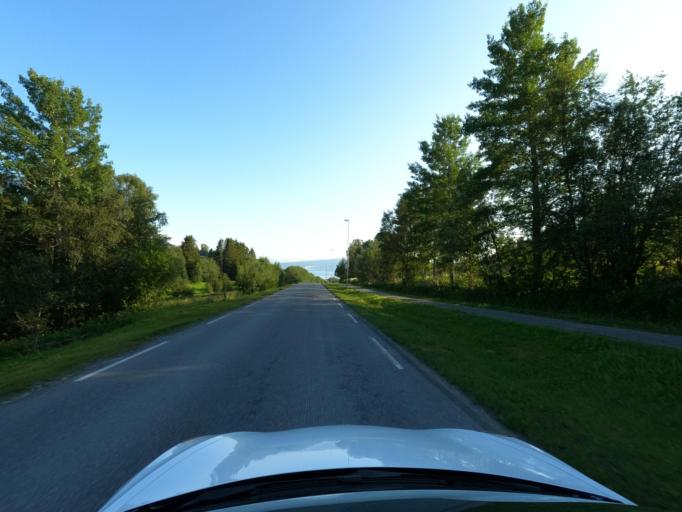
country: NO
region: Nordland
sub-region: Evenes
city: Randa
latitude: 68.4874
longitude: 16.8982
